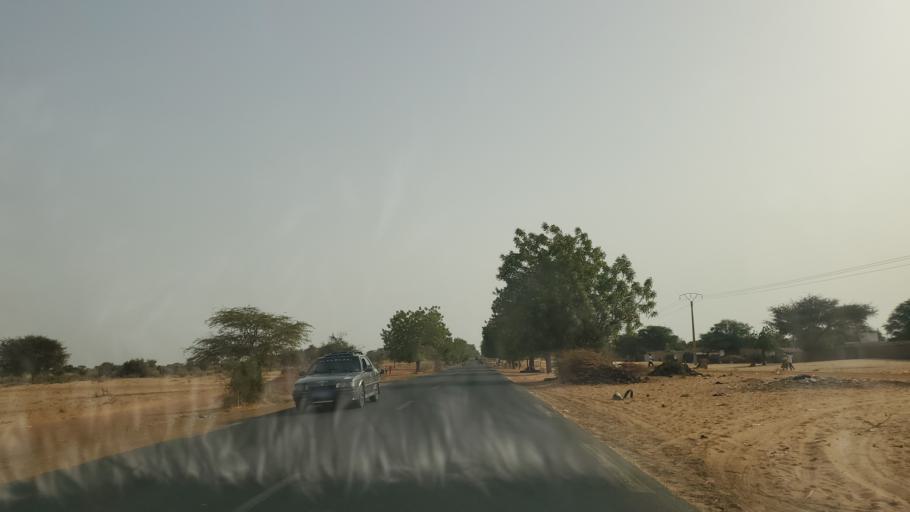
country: SN
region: Louga
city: Gueoul
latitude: 15.4387
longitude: -16.3881
